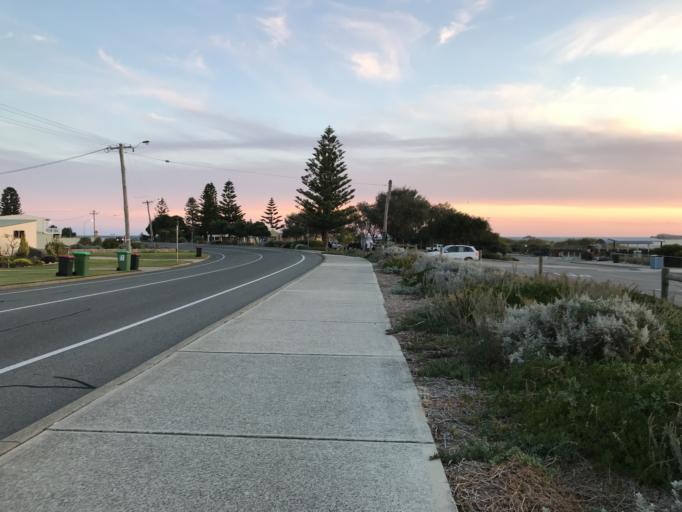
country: AU
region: Western Australia
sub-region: Rockingham
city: Shoalwater
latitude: -32.3030
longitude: 115.7026
